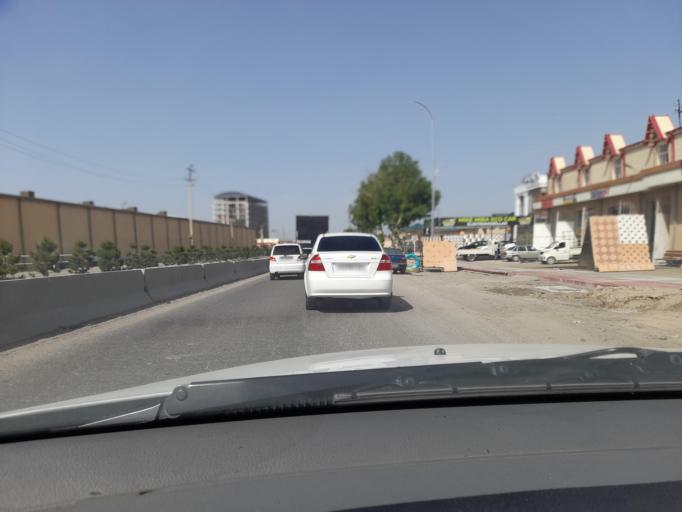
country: UZ
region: Samarqand
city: Samarqand
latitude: 39.6846
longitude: 67.0061
